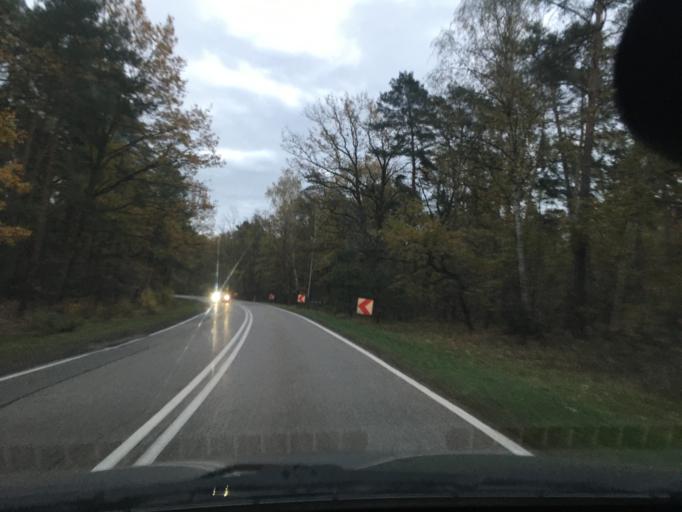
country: PL
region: Masovian Voivodeship
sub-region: Powiat pruszkowski
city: Nadarzyn
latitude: 52.0998
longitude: 20.8446
